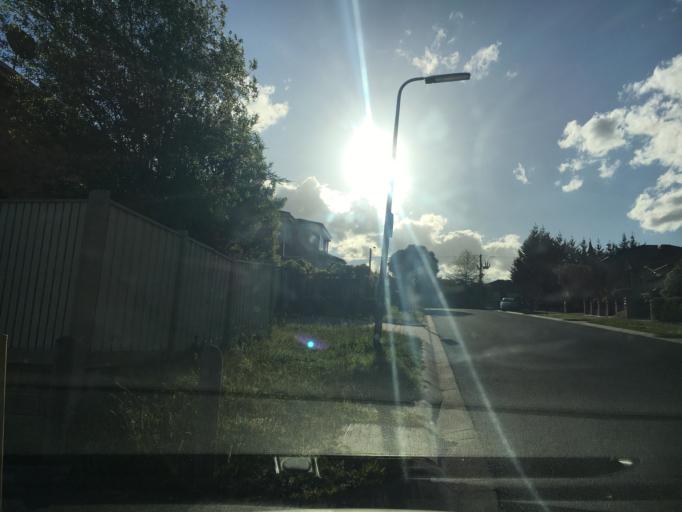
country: AU
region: Victoria
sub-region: Whitehorse
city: Vermont South
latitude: -37.8846
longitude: 145.1784
